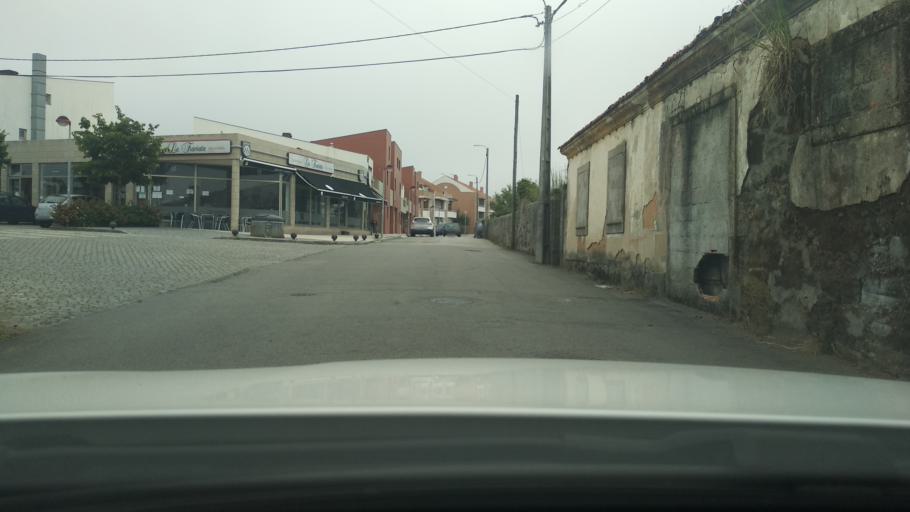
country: PT
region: Aveiro
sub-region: Espinho
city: Silvalde
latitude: 40.9946
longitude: -8.6277
